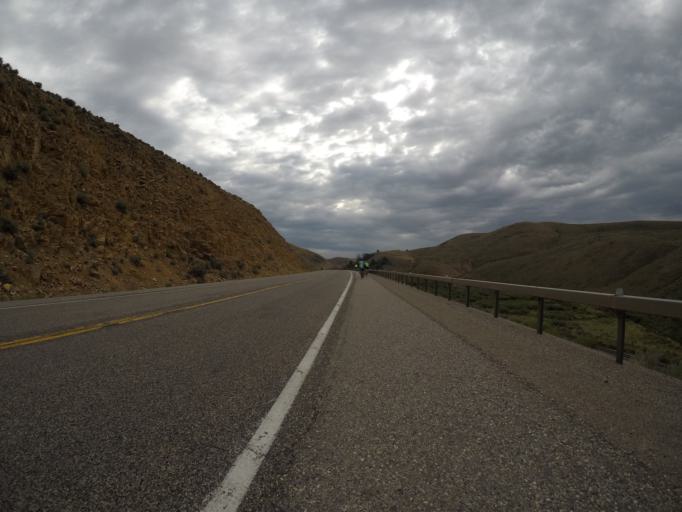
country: US
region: Wyoming
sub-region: Lincoln County
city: Kemmerer
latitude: 41.8229
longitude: -110.8598
